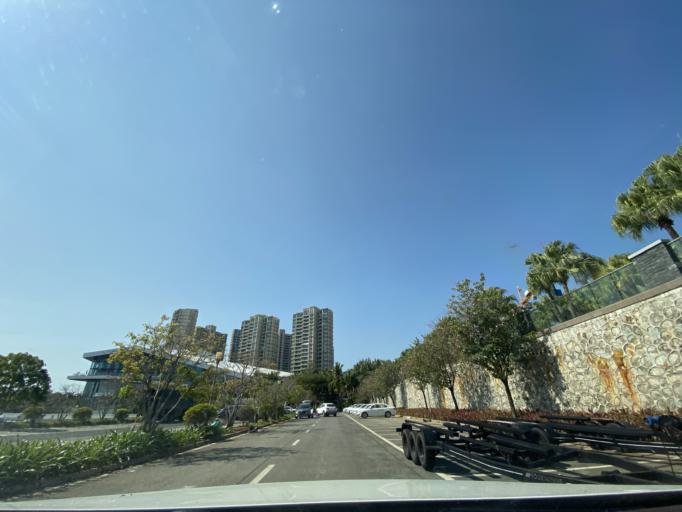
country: CN
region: Hainan
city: Yingzhou
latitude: 18.4090
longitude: 109.8721
